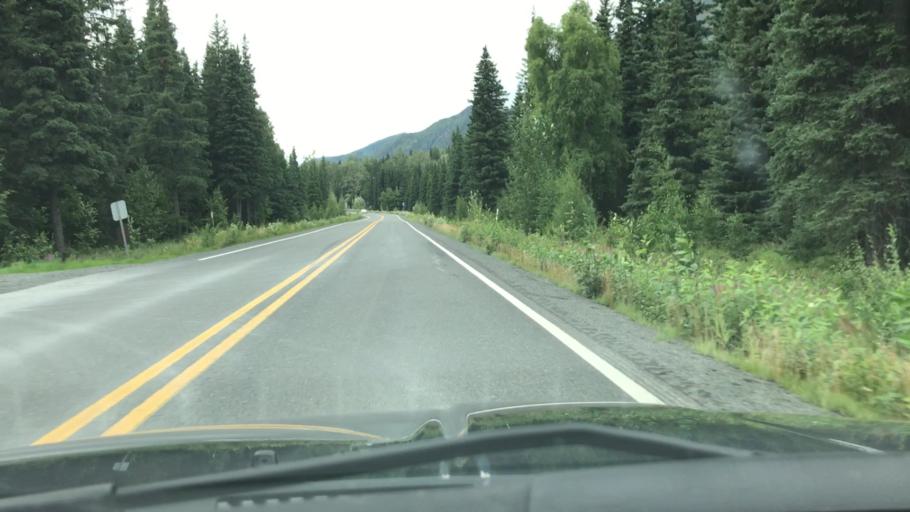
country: US
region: Alaska
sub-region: Kenai Peninsula Borough
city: Seward
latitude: 60.4834
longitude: -149.9418
